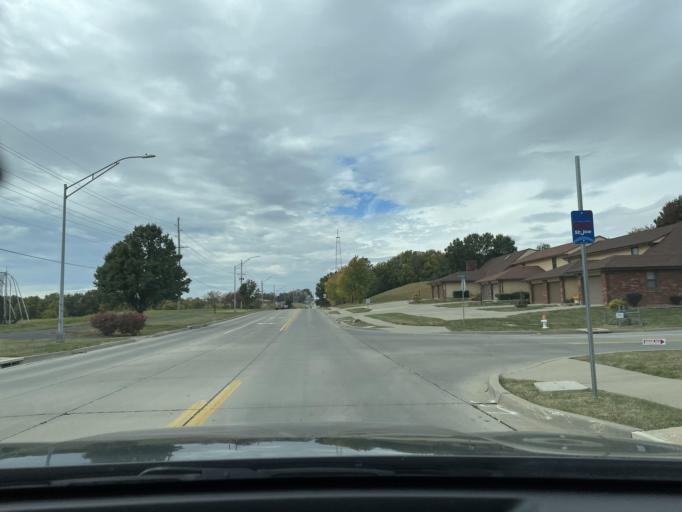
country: US
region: Missouri
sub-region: Buchanan County
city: Saint Joseph
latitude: 39.7699
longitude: -94.7849
